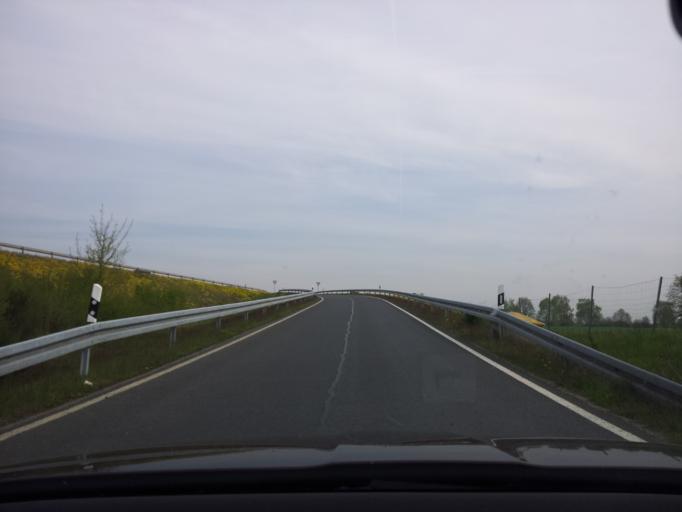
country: DE
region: Brandenburg
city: Luckau
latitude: 51.8536
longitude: 13.6870
